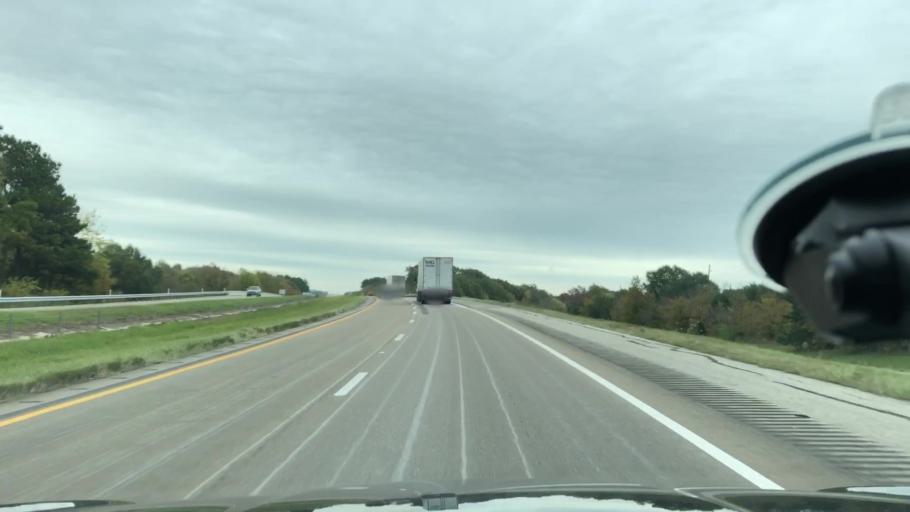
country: US
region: Texas
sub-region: Titus County
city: Mount Pleasant
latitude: 33.1583
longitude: -95.0367
